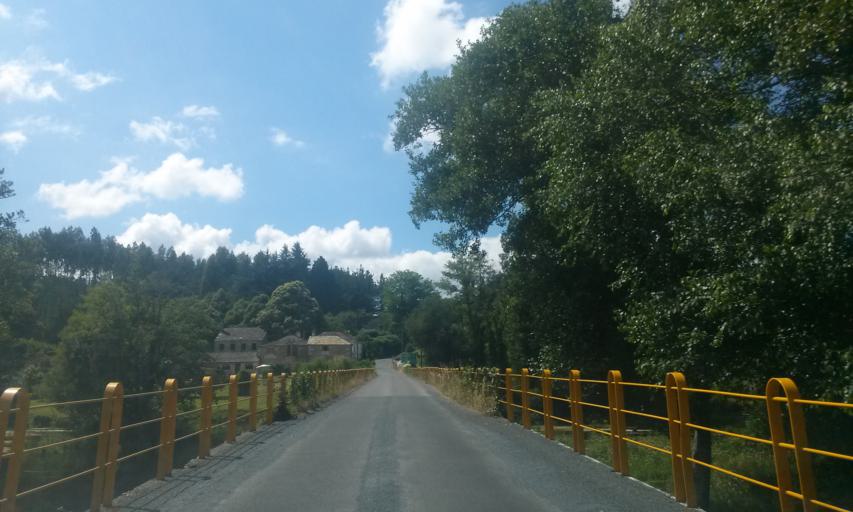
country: ES
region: Galicia
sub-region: Provincia de Lugo
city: Rabade
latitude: 43.1160
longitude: -7.6563
